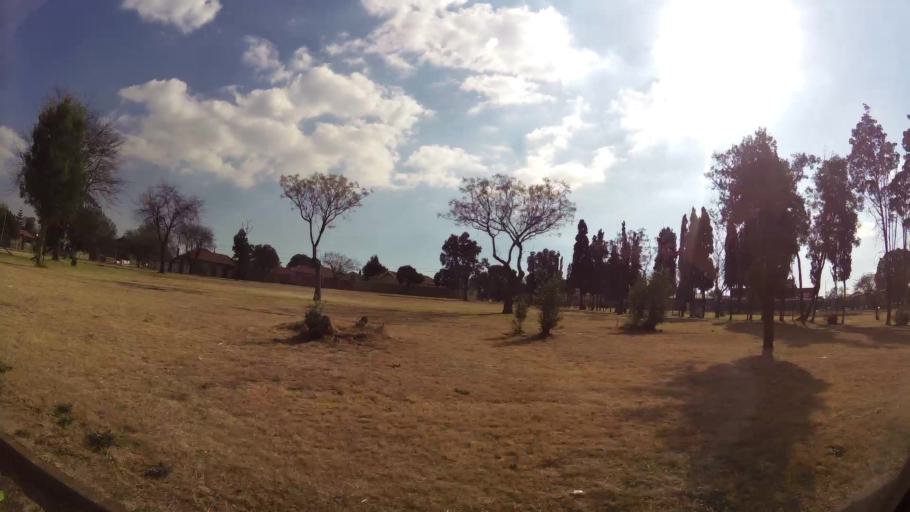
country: ZA
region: Gauteng
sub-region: Ekurhuleni Metropolitan Municipality
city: Germiston
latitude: -26.1762
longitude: 28.1812
